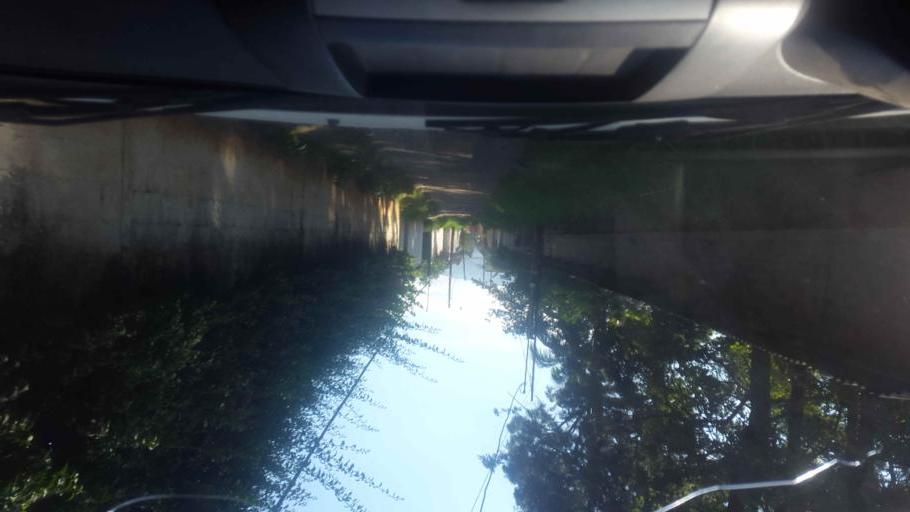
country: GT
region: Guatemala
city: Petapa
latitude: 14.5132
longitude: -90.5401
